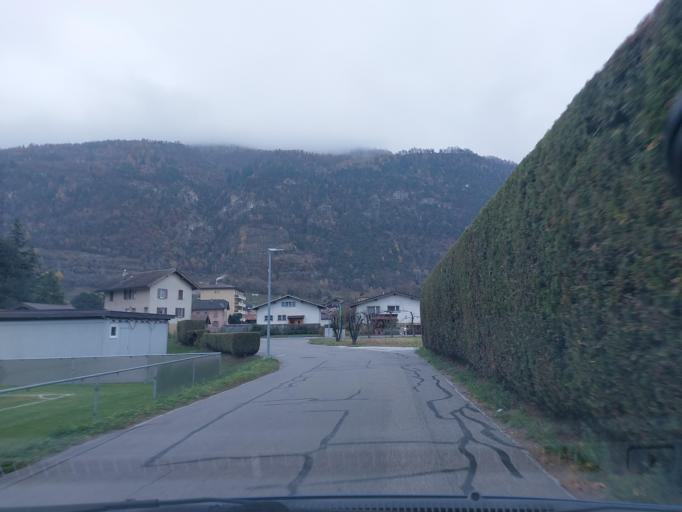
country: CH
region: Valais
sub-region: Sierre District
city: Grone
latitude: 46.2542
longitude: 7.4575
